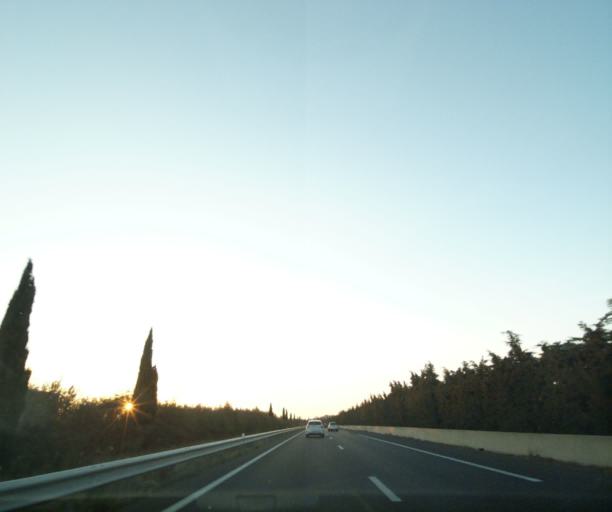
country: FR
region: Provence-Alpes-Cote d'Azur
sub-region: Departement des Bouches-du-Rhone
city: Mouries
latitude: 43.6388
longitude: 4.9123
